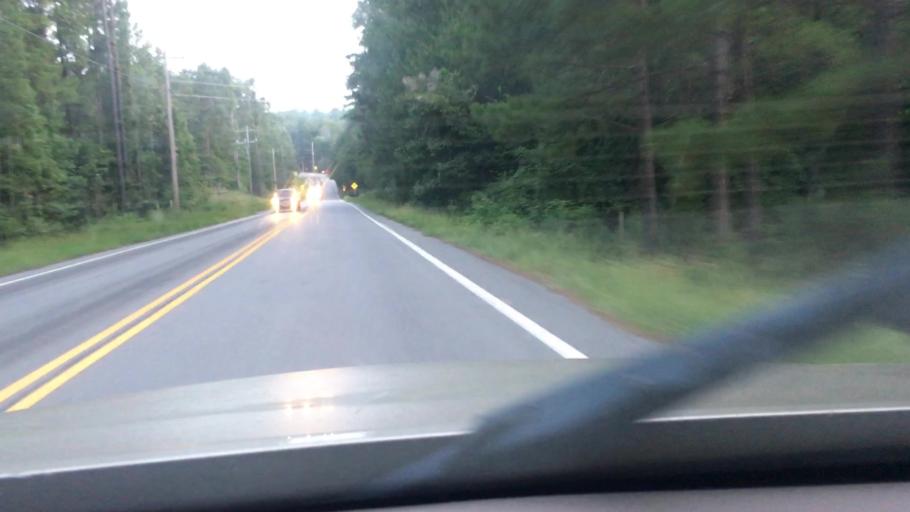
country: US
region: South Carolina
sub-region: Lexington County
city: Irmo
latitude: 34.1449
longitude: -81.1928
